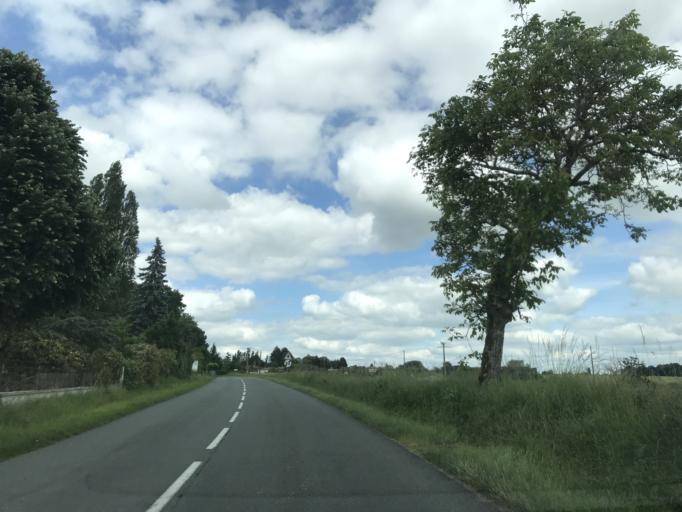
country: FR
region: Poitou-Charentes
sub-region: Departement de la Charente
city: Chalais
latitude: 45.2696
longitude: 0.0598
